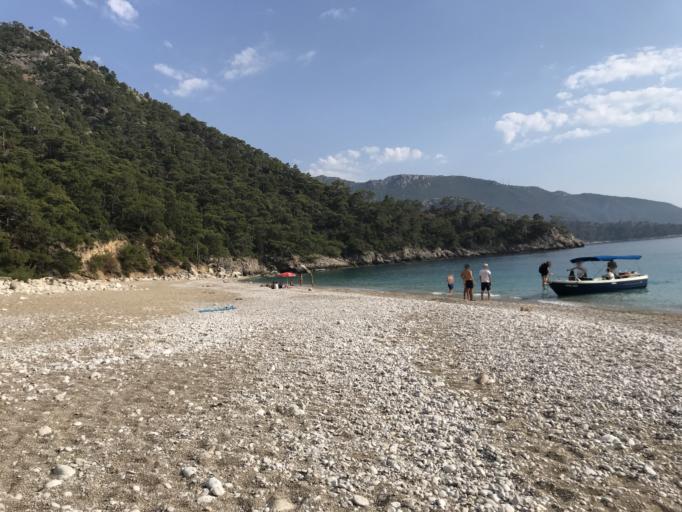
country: TR
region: Mugla
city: OEluedeniz
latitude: 36.4419
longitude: 29.1308
